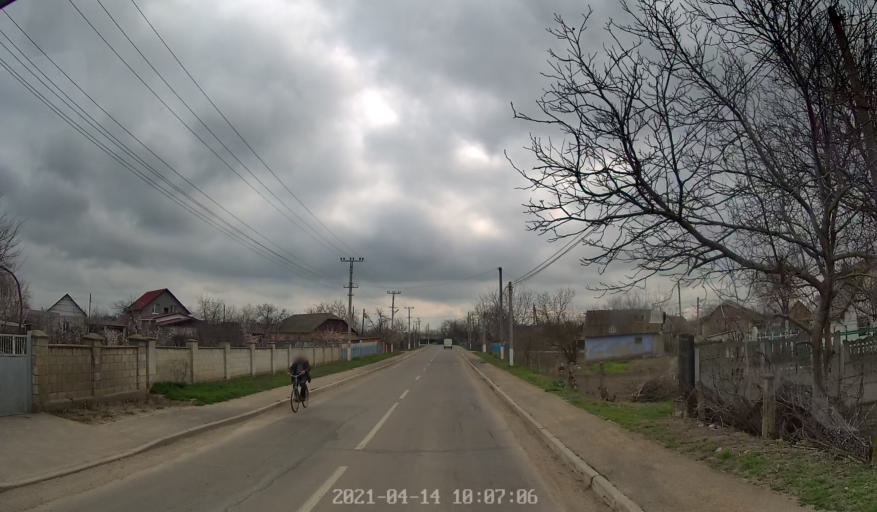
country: MD
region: Chisinau
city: Vadul lui Voda
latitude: 47.1433
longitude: 29.1258
